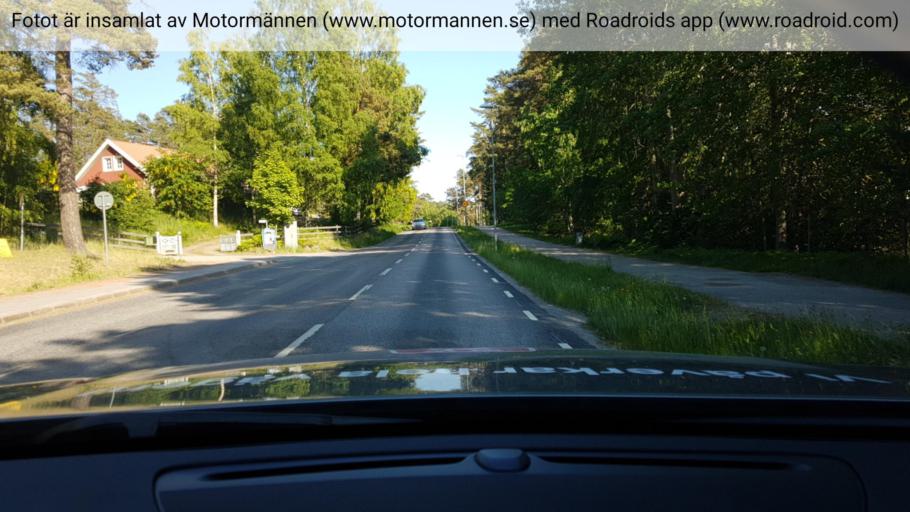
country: SE
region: Stockholm
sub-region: Varmdo Kommun
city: Holo
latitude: 59.2872
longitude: 18.6898
